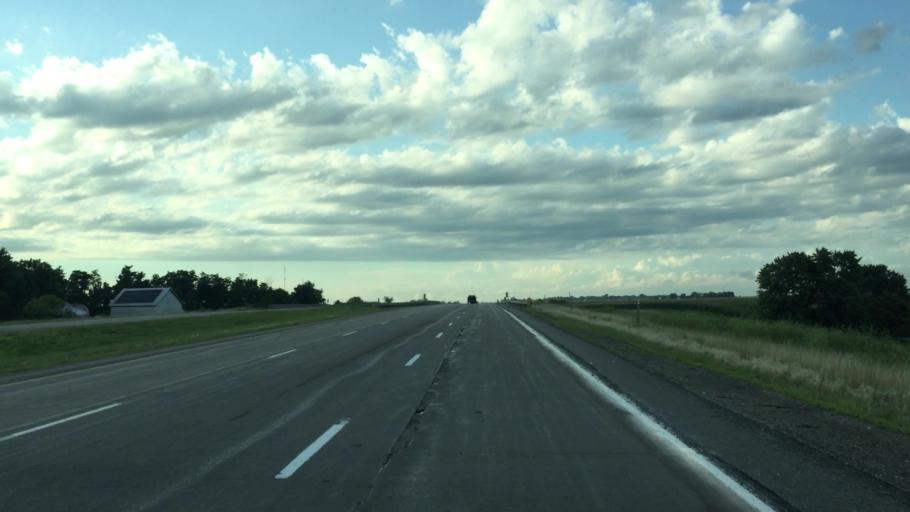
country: US
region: Iowa
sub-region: Washington County
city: Washington
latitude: 41.2920
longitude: -91.5337
